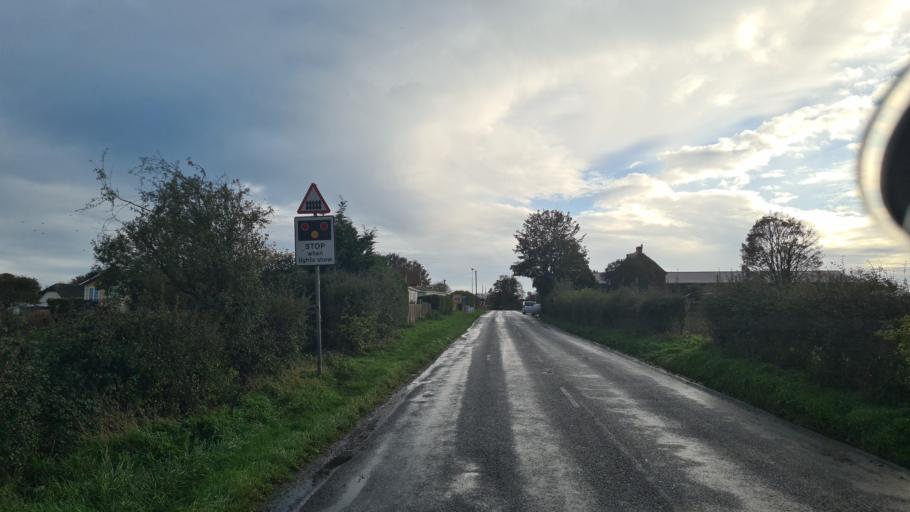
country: GB
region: England
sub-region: West Sussex
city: Arundel
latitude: 50.8310
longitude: -0.5768
